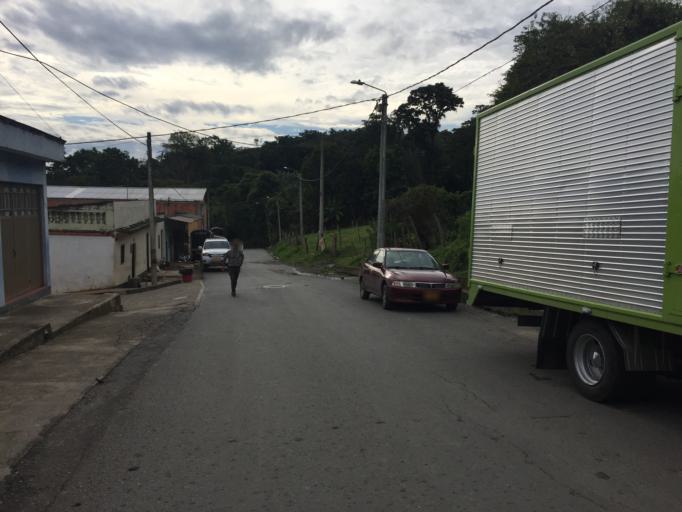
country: CO
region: Santander
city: Guepsa
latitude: 6.0172
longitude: -73.5466
